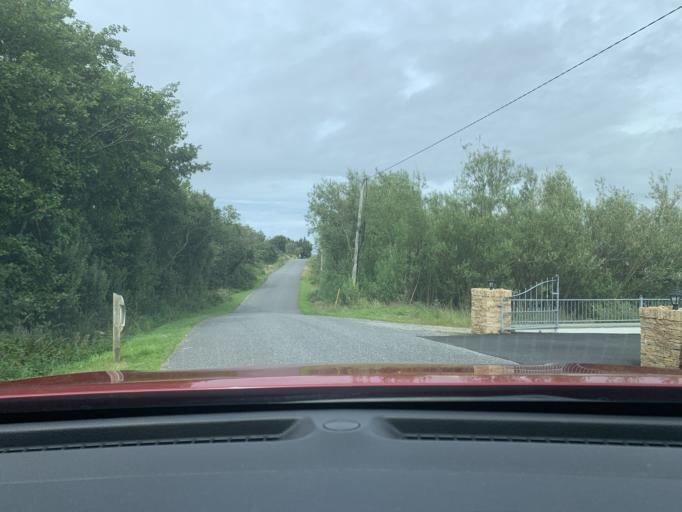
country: IE
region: Ulster
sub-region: County Donegal
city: Dungloe
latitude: 54.9407
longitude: -8.3592
